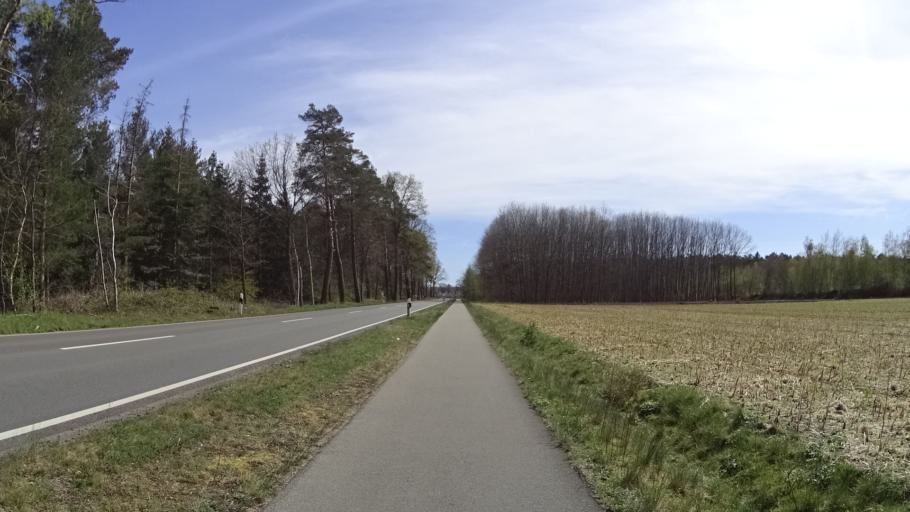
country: DE
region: Lower Saxony
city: Spelle
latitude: 52.3402
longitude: 7.4502
